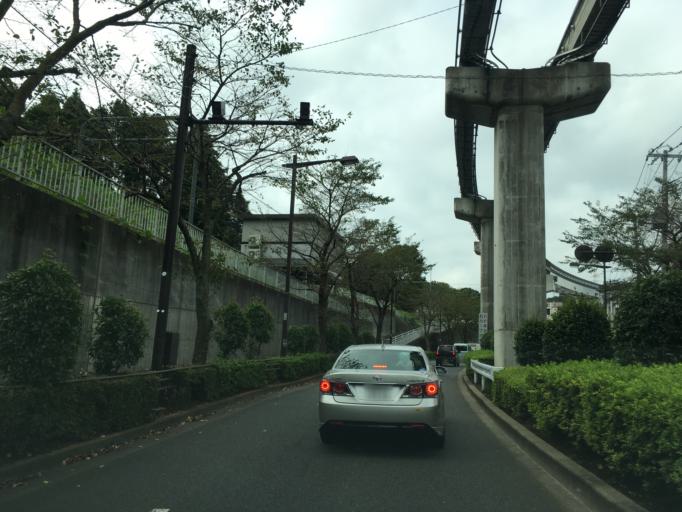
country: JP
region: Tokyo
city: Hino
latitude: 35.6517
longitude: 139.4083
